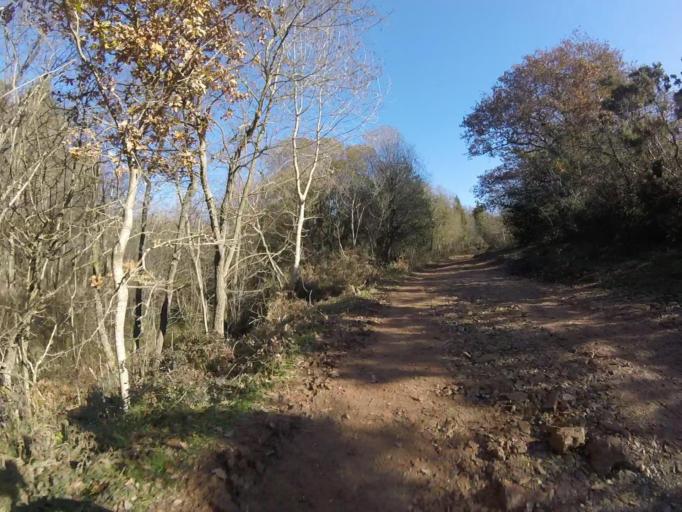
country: ES
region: Navarre
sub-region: Provincia de Navarra
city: Bera
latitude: 43.3195
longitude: -1.7021
